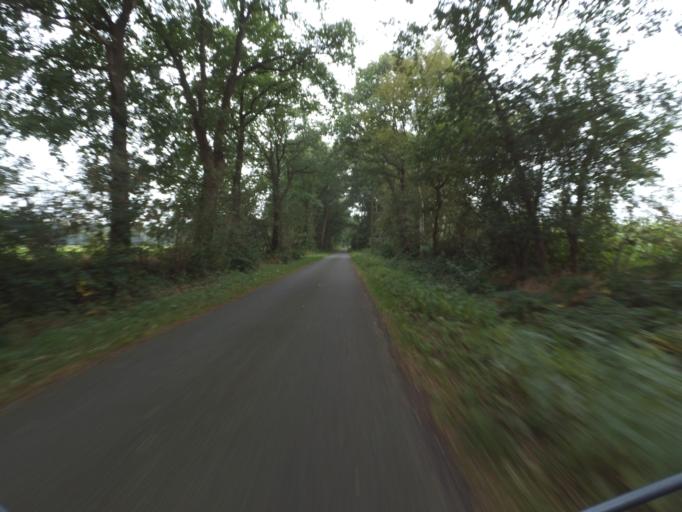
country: DE
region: Lower Saxony
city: Isterberg
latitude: 52.3383
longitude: 7.0606
